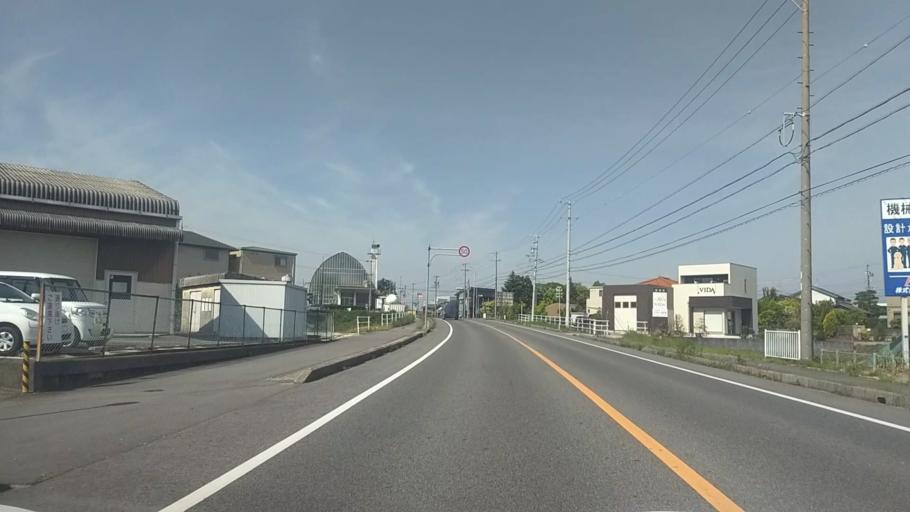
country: JP
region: Aichi
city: Anjo
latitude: 34.9495
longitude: 137.1013
